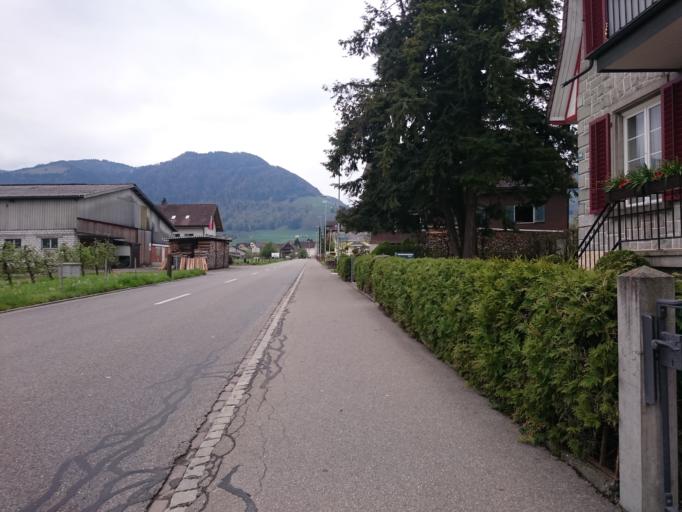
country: CH
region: Schwyz
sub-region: Bezirk March
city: Schubelbach
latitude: 47.1861
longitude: 8.8976
